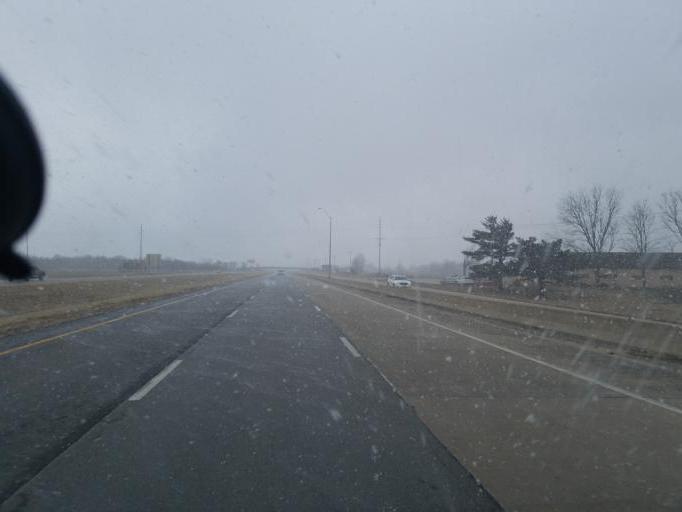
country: US
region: Missouri
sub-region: Randolph County
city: Moberly
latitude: 39.4400
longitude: -92.4218
